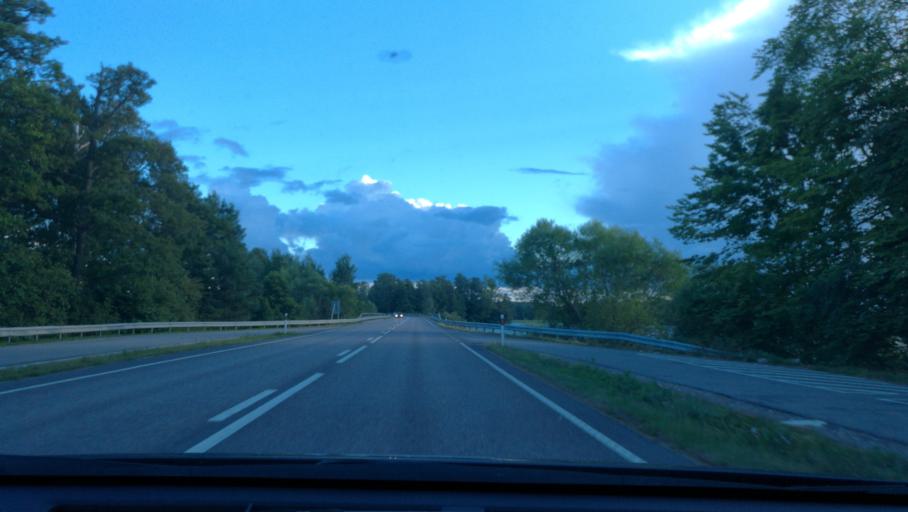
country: SE
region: Vaestmanland
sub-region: Kungsors Kommun
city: Kungsoer
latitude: 59.2482
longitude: 16.1060
